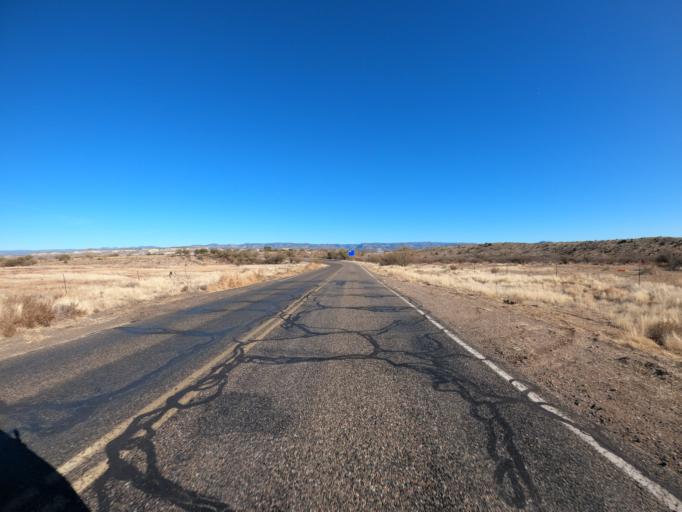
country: US
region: Arizona
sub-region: Yavapai County
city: Camp Verde
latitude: 34.5563
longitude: -111.8793
